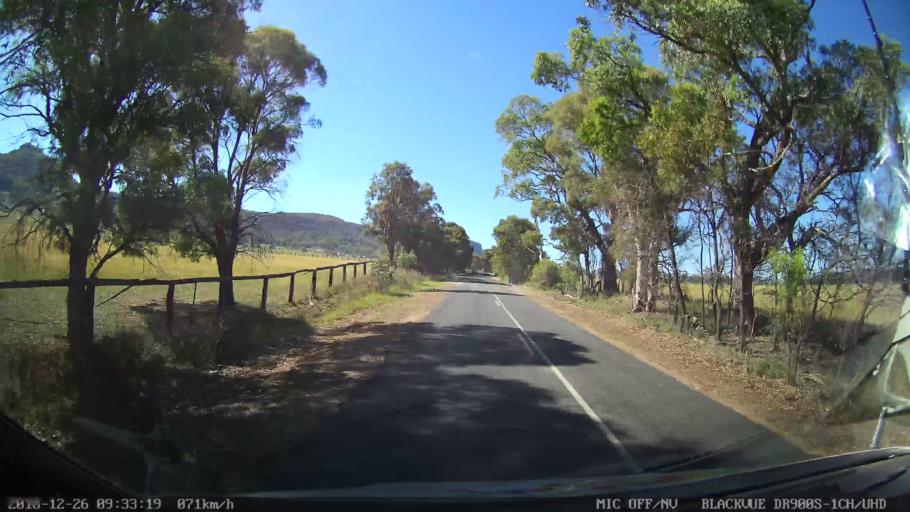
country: AU
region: New South Wales
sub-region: Mid-Western Regional
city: Kandos
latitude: -32.8934
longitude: 150.0345
